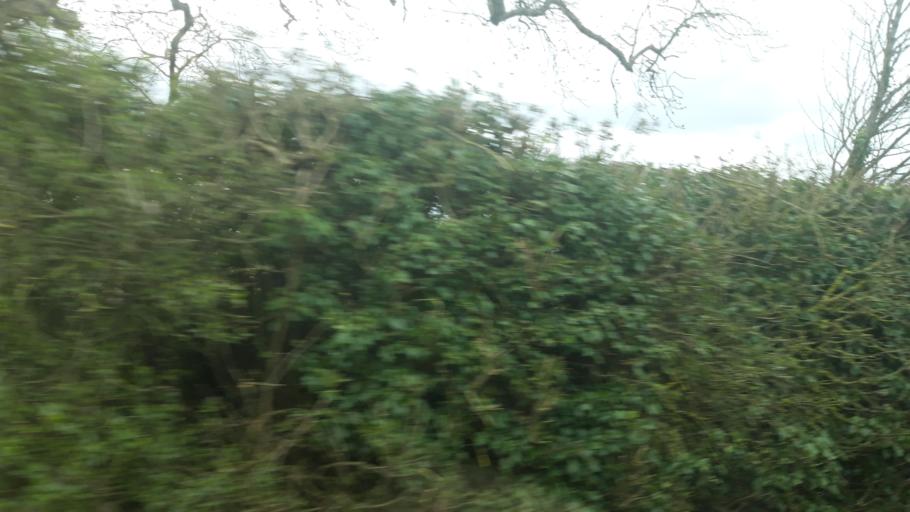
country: IE
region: Leinster
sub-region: Kildare
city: Celbridge
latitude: 53.3606
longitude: -6.5657
